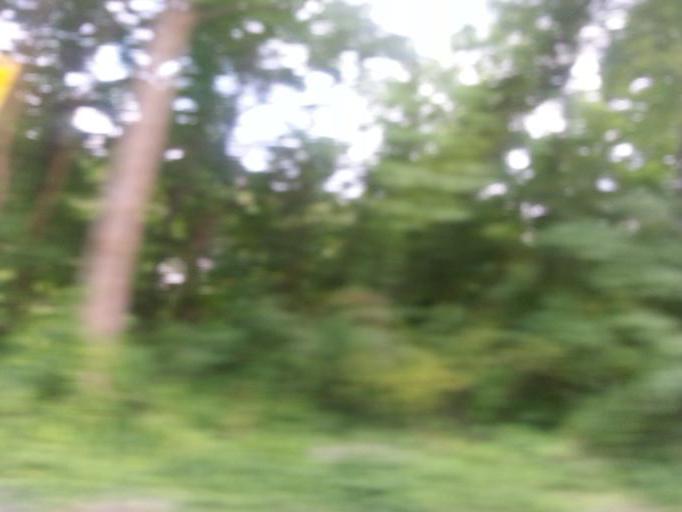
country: US
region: Tennessee
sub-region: Anderson County
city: Rocky Top
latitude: 36.1465
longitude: -84.2451
